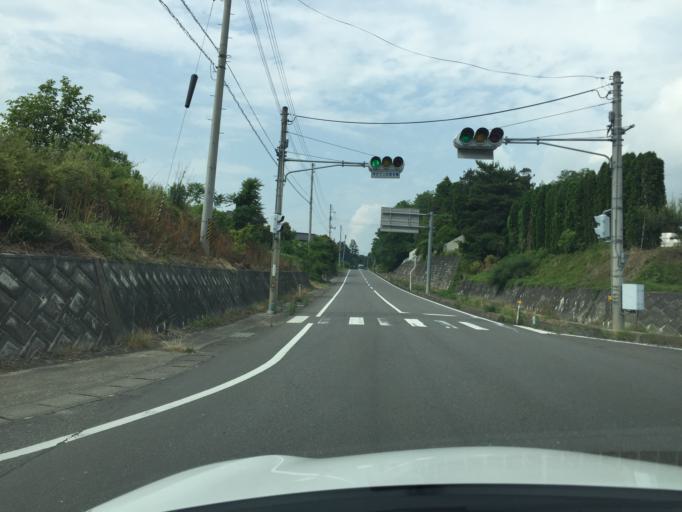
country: JP
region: Fukushima
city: Sukagawa
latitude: 37.2869
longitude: 140.4267
